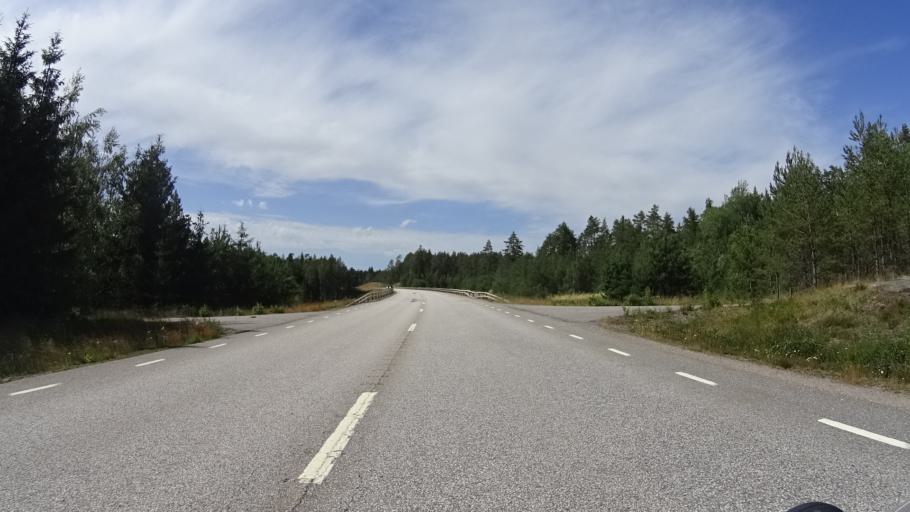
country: SE
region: Kalmar
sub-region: Vasterviks Kommun
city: Gamleby
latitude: 57.9562
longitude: 16.3741
